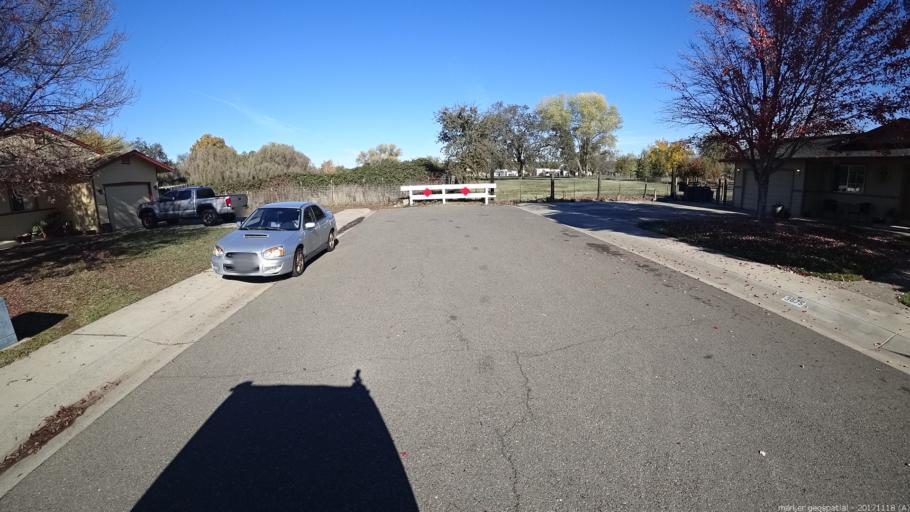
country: US
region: California
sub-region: Shasta County
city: Cottonwood
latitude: 40.3945
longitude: -122.2763
